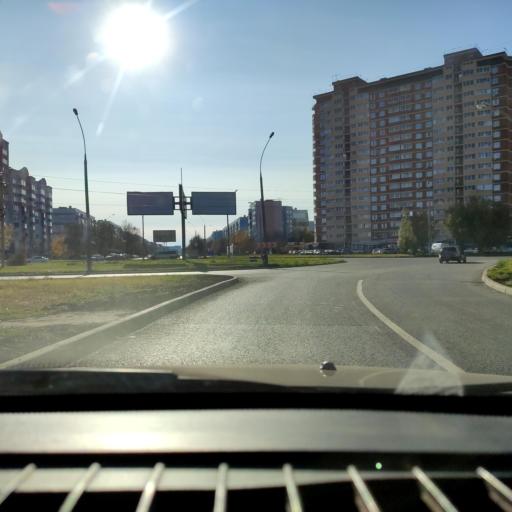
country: RU
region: Samara
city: Tol'yatti
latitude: 53.5431
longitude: 49.3309
